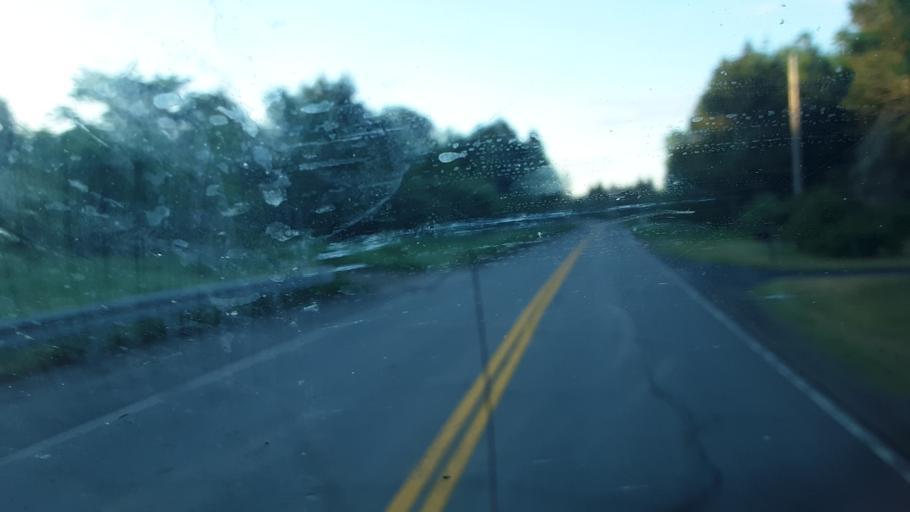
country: US
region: Maine
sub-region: Aroostook County
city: Presque Isle
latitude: 46.7540
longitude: -68.0586
